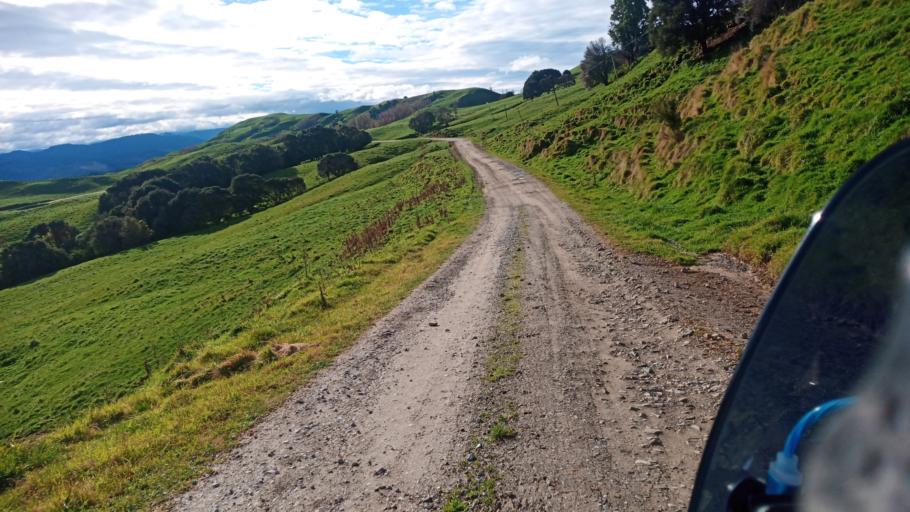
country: NZ
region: Gisborne
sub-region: Gisborne District
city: Gisborne
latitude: -38.3715
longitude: 177.9671
